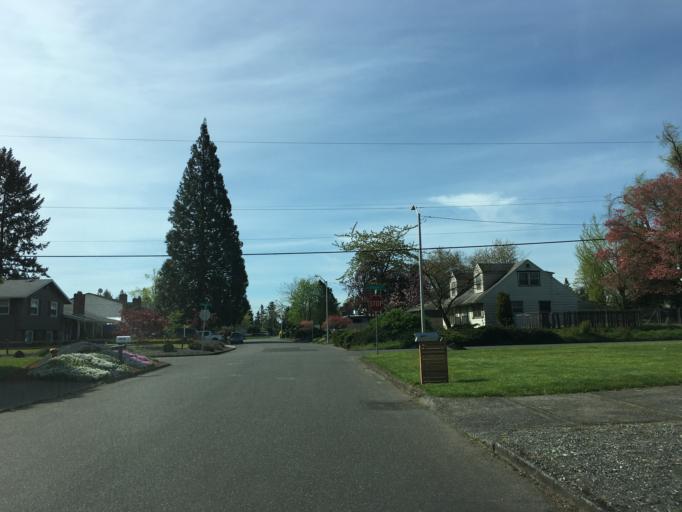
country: US
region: Oregon
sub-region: Multnomah County
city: Lents
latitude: 45.5357
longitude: -122.5332
